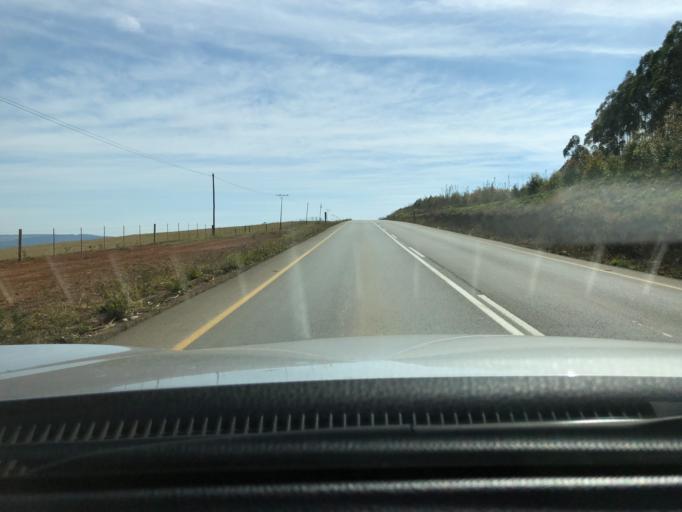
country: ZA
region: KwaZulu-Natal
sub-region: Sisonke District Municipality
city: Ixopo
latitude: -30.1794
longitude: 30.0598
